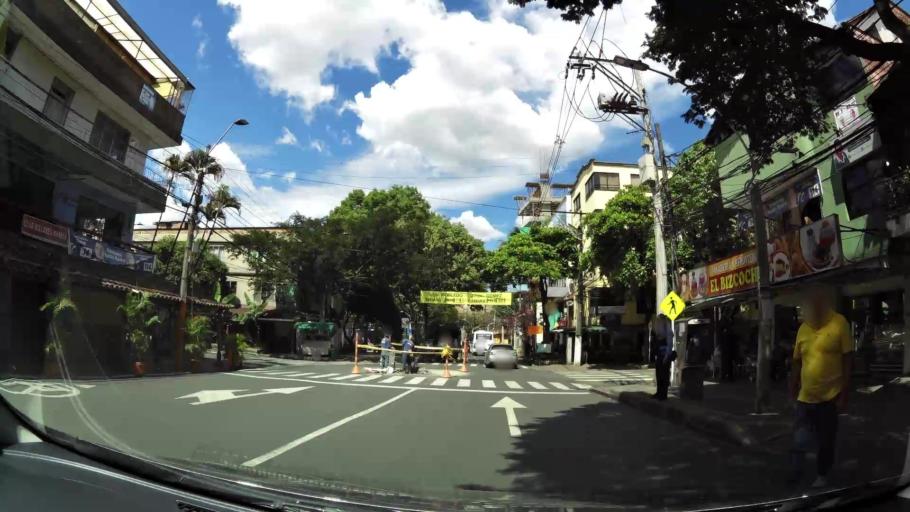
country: CO
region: Antioquia
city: Sabaneta
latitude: 6.1505
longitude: -75.6167
